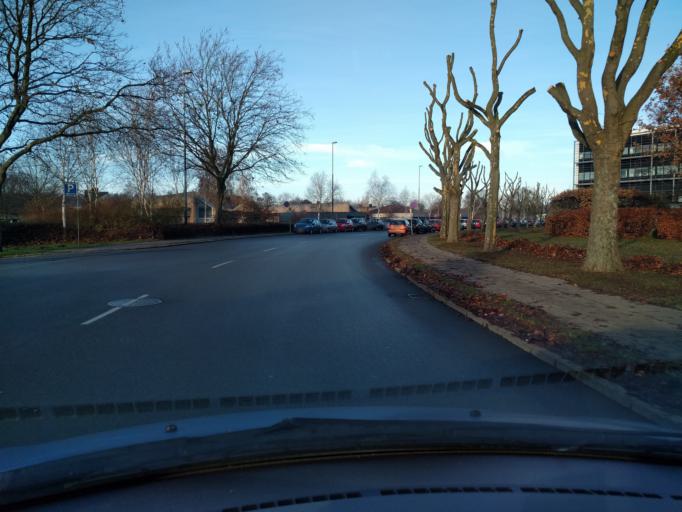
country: DK
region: South Denmark
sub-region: Odense Kommune
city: Odense
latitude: 55.3859
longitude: 10.3628
